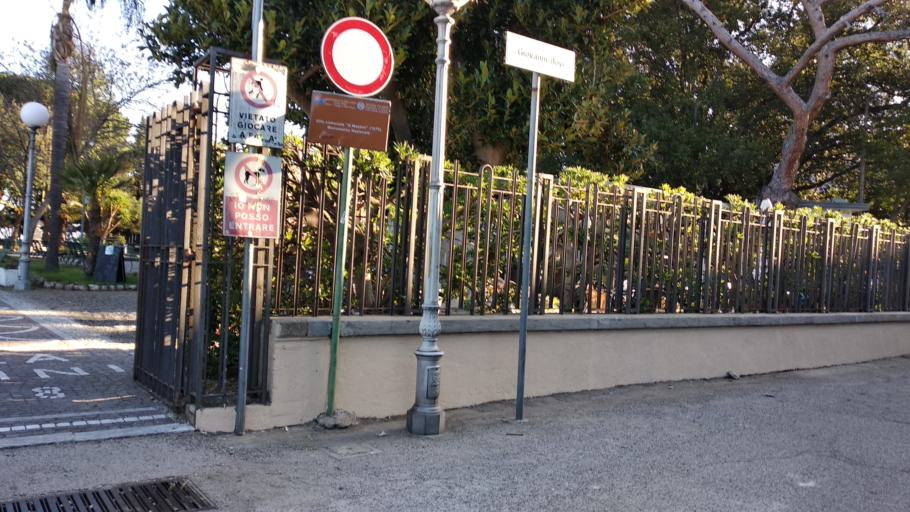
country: IT
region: Calabria
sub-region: Provincia di Reggio Calabria
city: Seminara
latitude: 38.3564
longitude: 15.8445
